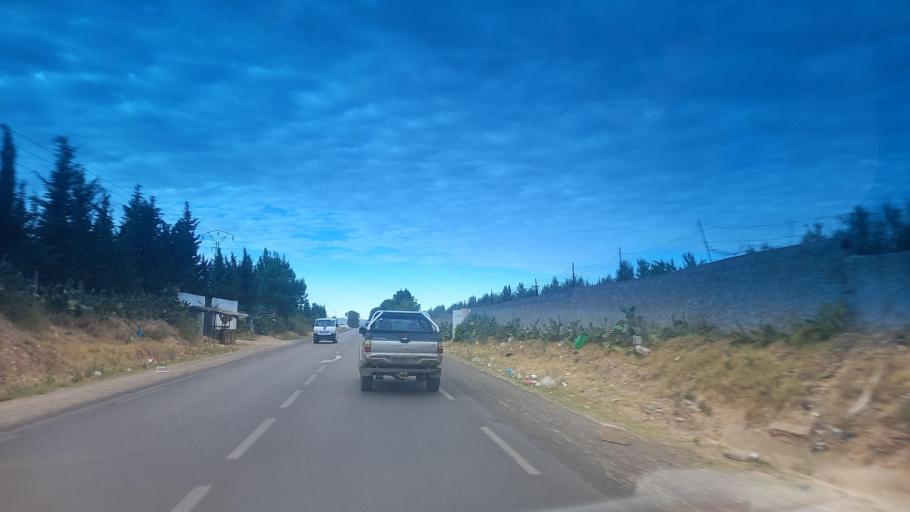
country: TN
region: Al Qasrayn
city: Sbiba
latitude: 35.2768
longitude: 9.0937
